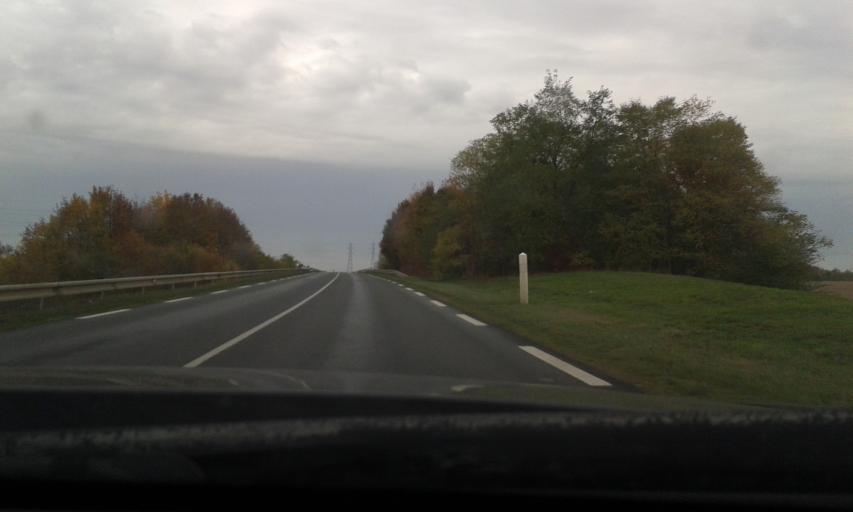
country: FR
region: Centre
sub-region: Departement d'Eure-et-Loir
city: Baigneaux
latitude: 48.1277
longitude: 1.8546
